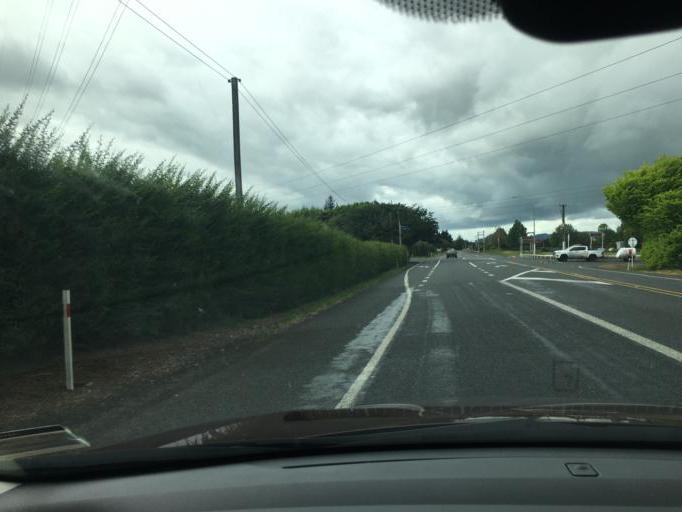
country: NZ
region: Waikato
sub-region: Waipa District
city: Cambridge
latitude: -37.9075
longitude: 175.4508
